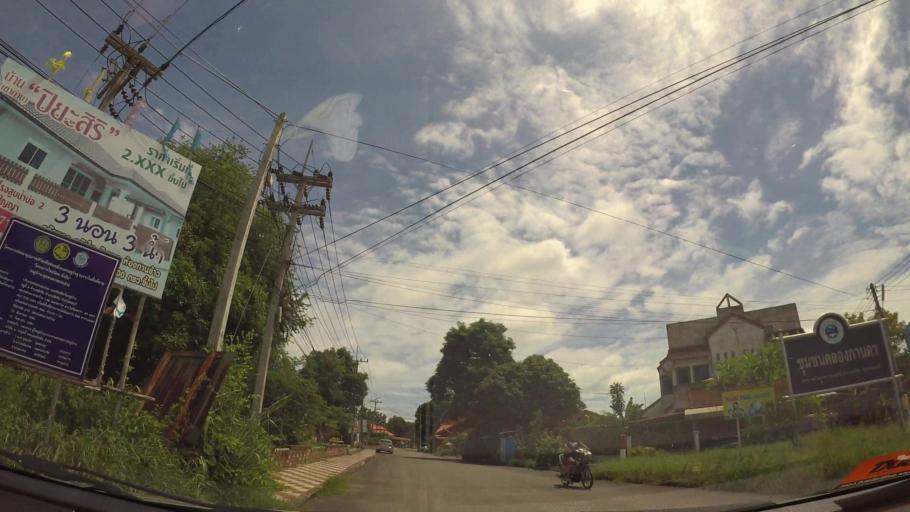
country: TH
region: Chon Buri
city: Sattahip
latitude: 12.7053
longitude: 100.8856
